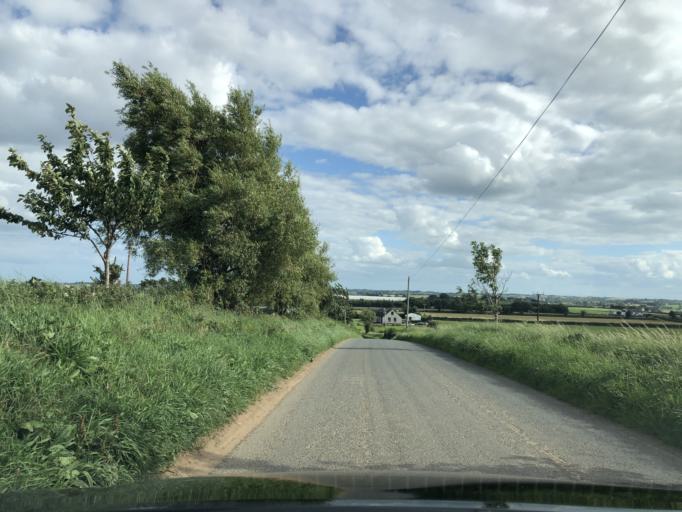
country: GB
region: Northern Ireland
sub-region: Ards District
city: Newtownards
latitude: 54.5629
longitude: -5.7102
